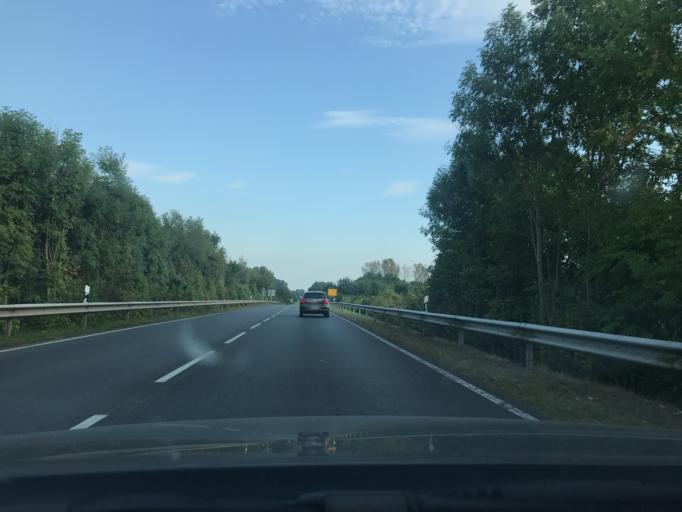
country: DE
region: North Rhine-Westphalia
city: Geldern
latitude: 51.5050
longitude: 6.3053
